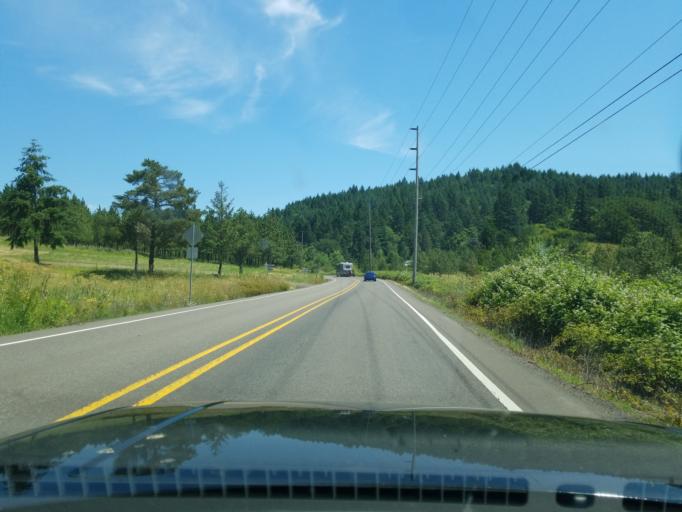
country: US
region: Oregon
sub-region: Yamhill County
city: Yamhill
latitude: 45.3819
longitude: -123.1433
